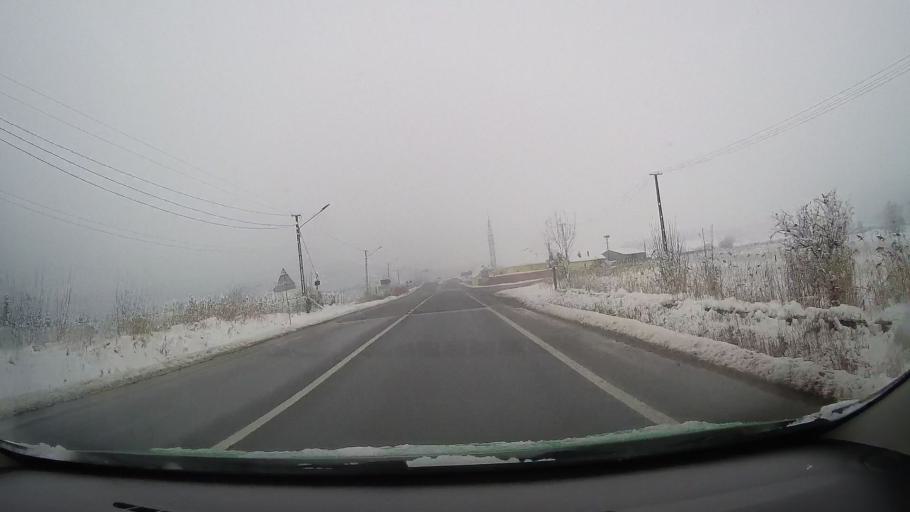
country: RO
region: Sibiu
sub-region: Comuna Orlat
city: Orlat
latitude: 45.7825
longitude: 23.9433
